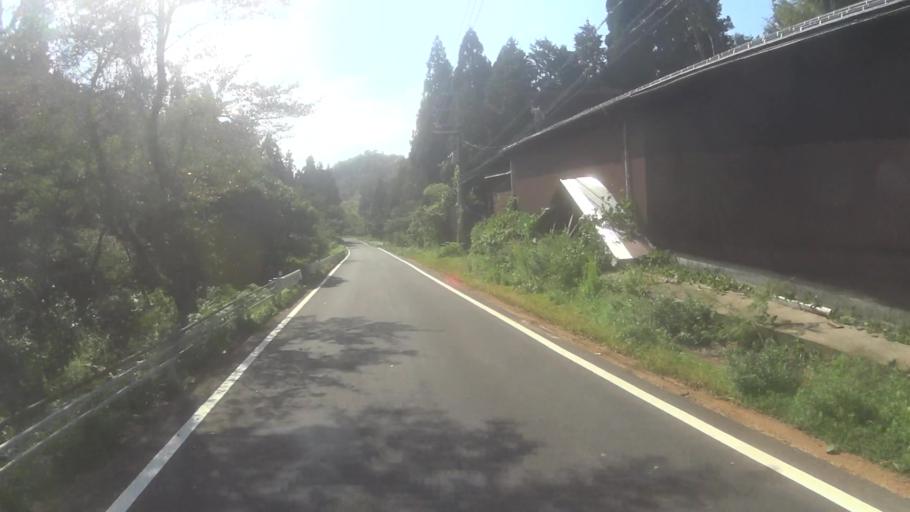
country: JP
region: Kyoto
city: Miyazu
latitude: 35.6875
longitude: 135.1144
